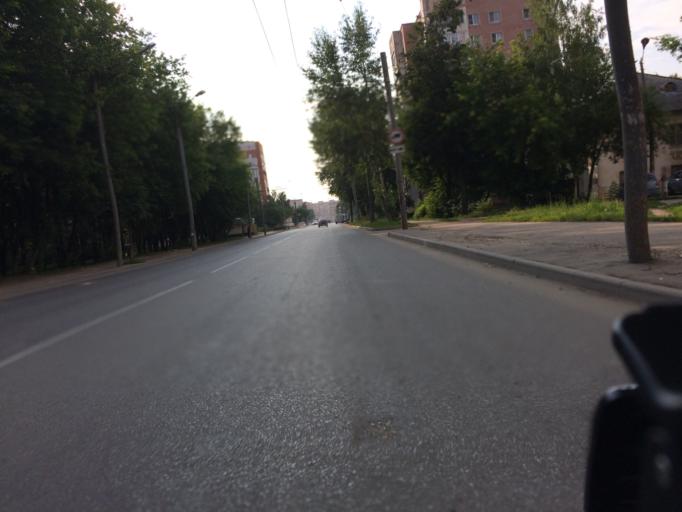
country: RU
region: Mariy-El
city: Yoshkar-Ola
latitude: 56.6348
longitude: 47.9419
